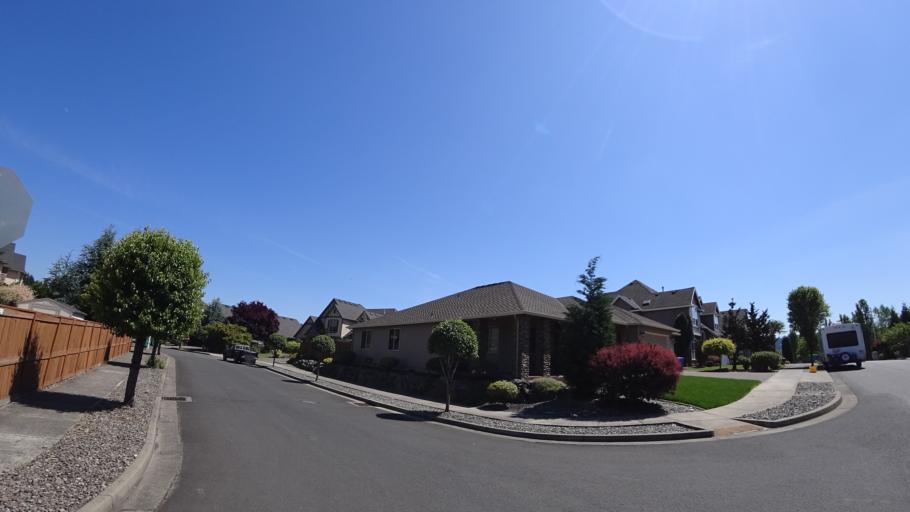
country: US
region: Oregon
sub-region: Clackamas County
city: Happy Valley
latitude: 45.4771
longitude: -122.4887
